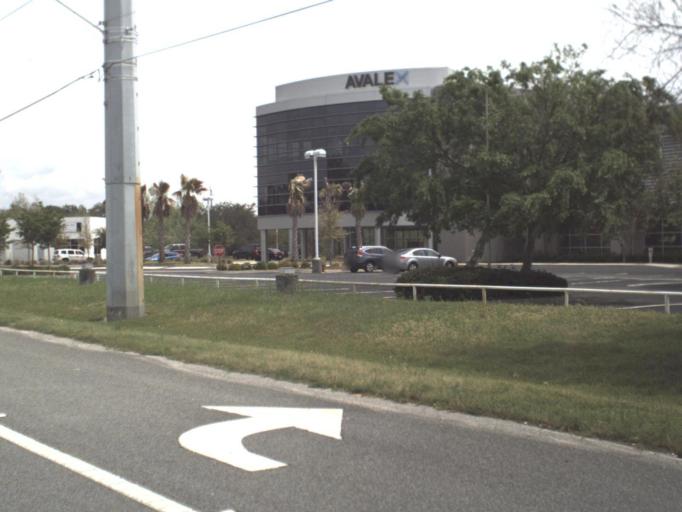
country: US
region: Florida
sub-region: Santa Rosa County
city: Oriole Beach
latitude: 30.3785
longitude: -87.1136
